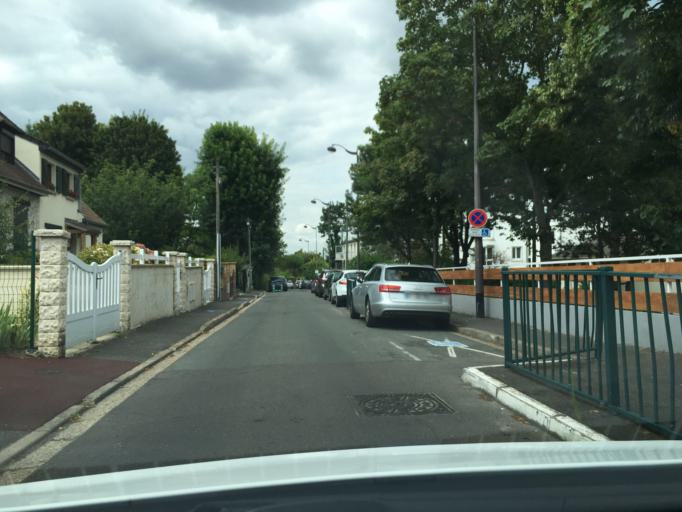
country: FR
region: Ile-de-France
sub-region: Departement des Hauts-de-Seine
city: Rueil-Malmaison
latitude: 48.8698
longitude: 2.1786
